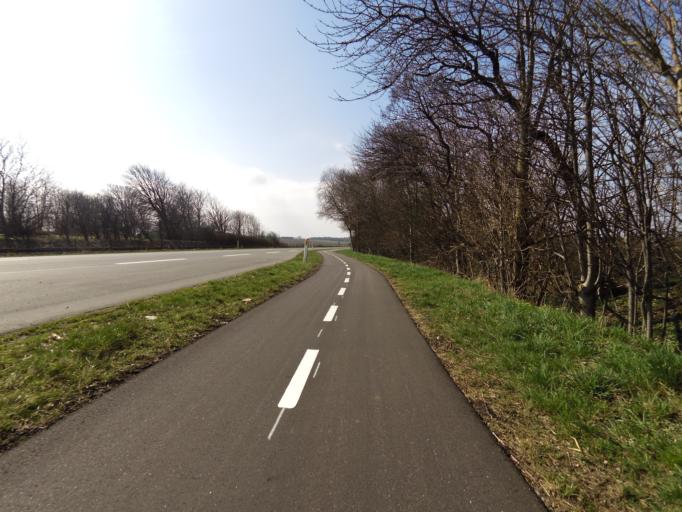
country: DK
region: Central Jutland
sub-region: Struer Kommune
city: Struer
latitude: 56.4661
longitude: 8.6841
